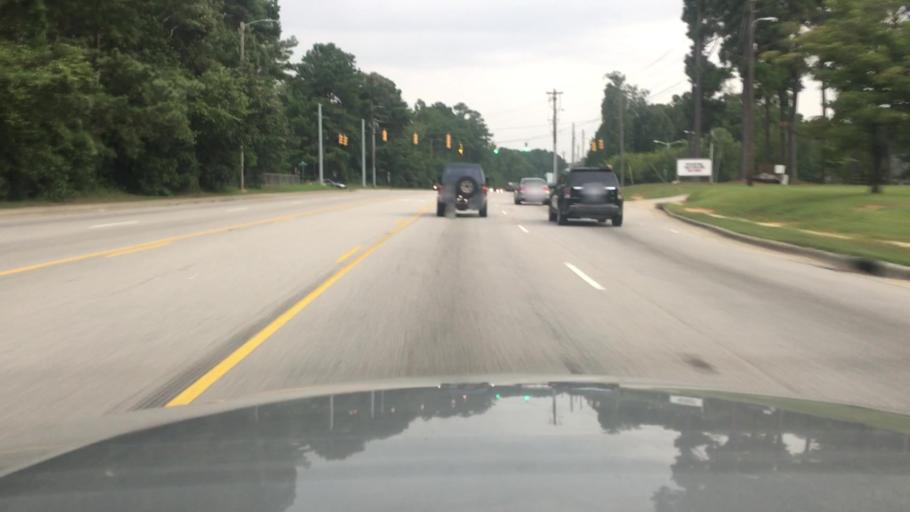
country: US
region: North Carolina
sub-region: Cumberland County
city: Fort Bragg
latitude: 35.0783
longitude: -79.0102
